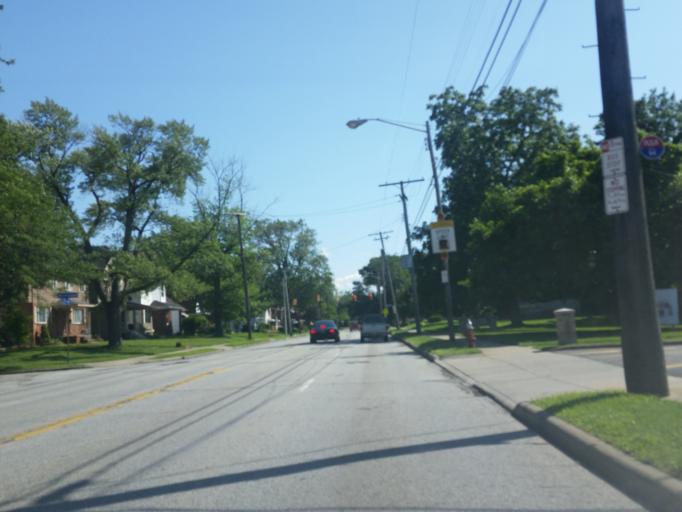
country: US
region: Ohio
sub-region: Cuyahoga County
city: Lakewood
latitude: 41.4664
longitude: -81.7986
